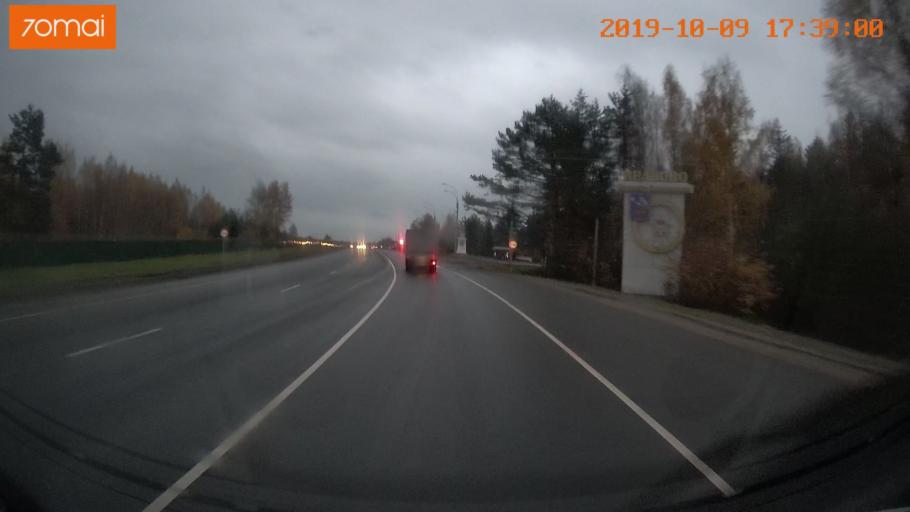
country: RU
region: Ivanovo
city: Bogorodskoye
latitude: 57.0647
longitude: 40.9533
